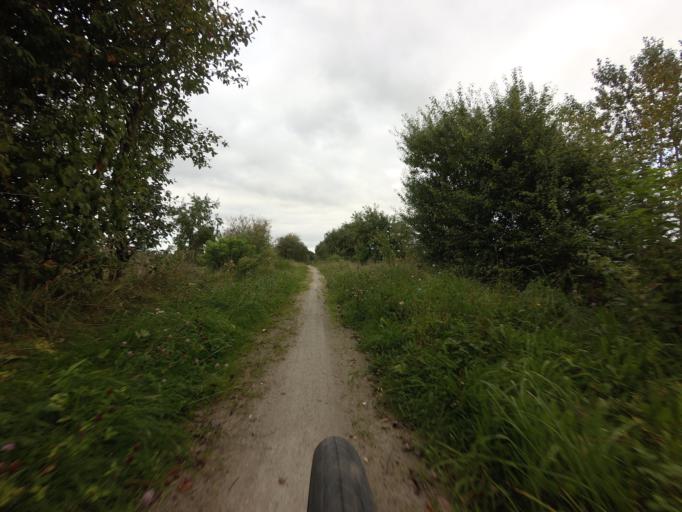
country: DK
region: South Denmark
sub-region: Billund Kommune
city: Billund
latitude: 55.8261
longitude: 9.0310
